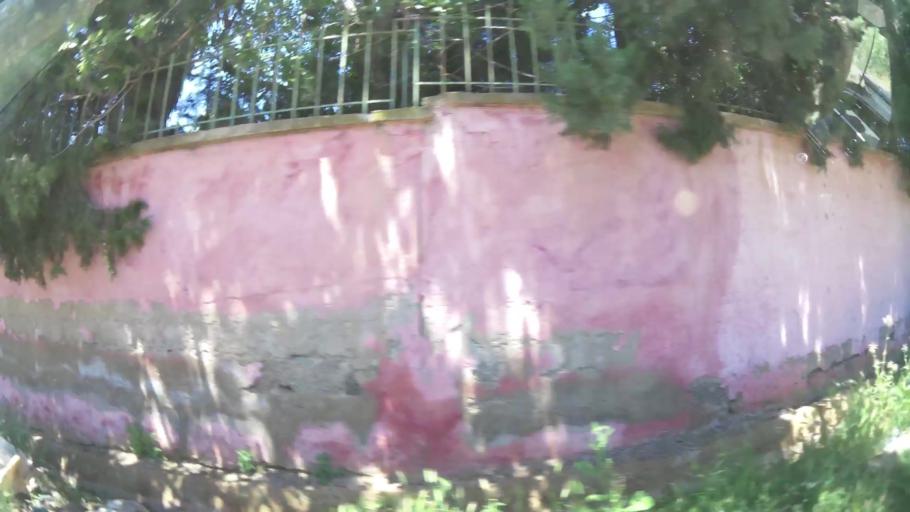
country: MA
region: Oriental
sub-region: Berkane-Taourirt
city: Madagh
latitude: 35.0739
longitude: -2.2155
